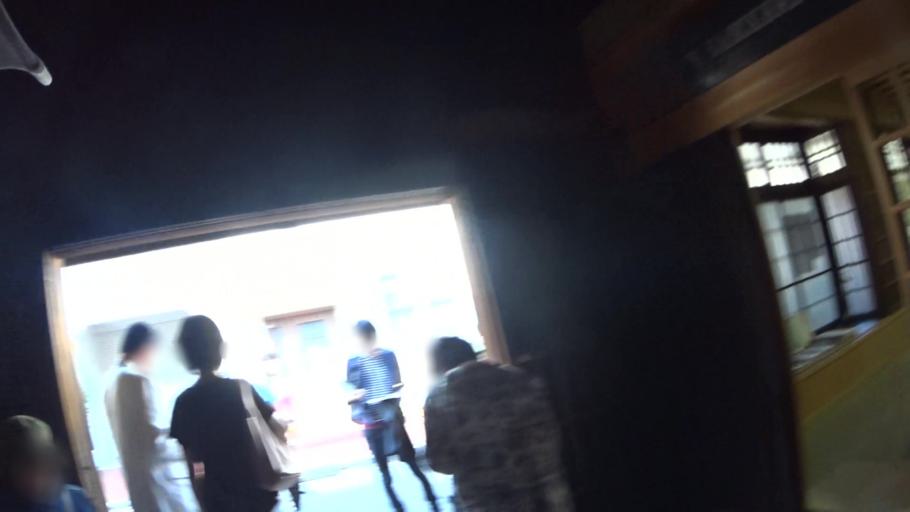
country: JP
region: Kyoto
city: Kyoto
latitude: 35.0100
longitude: 135.7813
